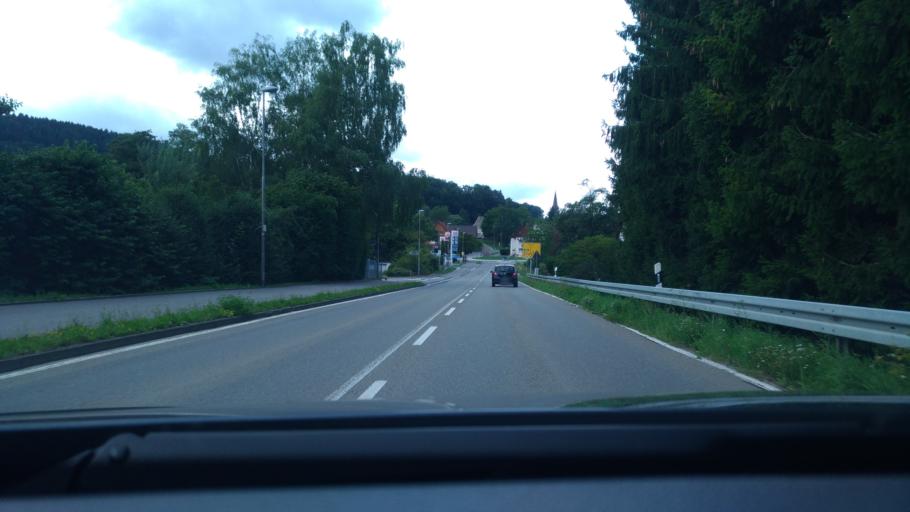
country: DE
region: Baden-Wuerttemberg
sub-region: Freiburg Region
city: Stockach
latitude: 47.8594
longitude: 9.0071
